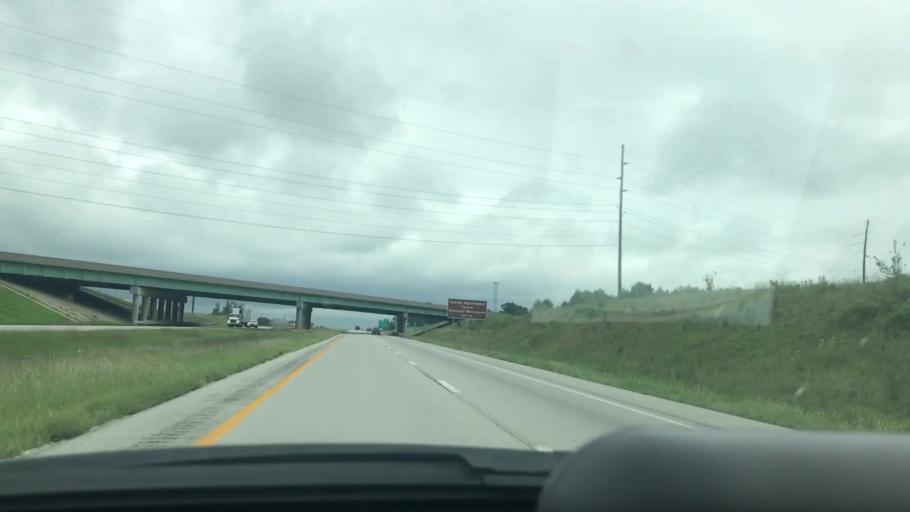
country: US
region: Missouri
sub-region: Jasper County
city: Duquesne
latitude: 37.0548
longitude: -94.4466
